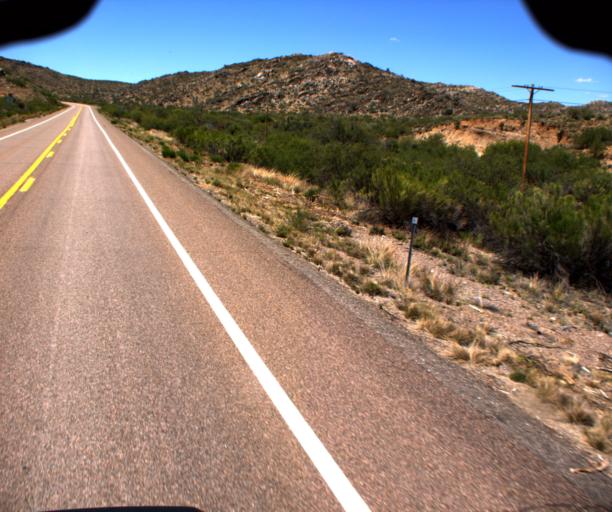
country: US
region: Arizona
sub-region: Yavapai County
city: Bagdad
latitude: 34.5286
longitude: -113.1361
